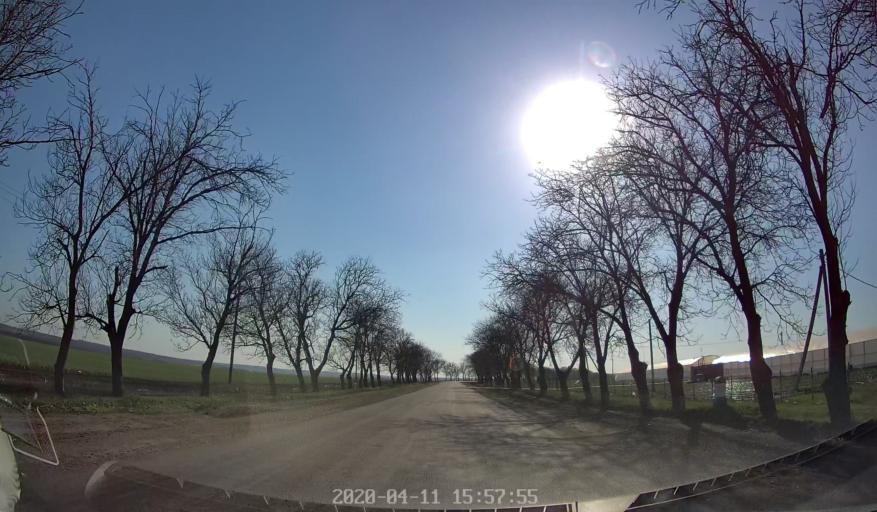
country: MD
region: Chisinau
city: Vadul lui Voda
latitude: 47.0870
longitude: 29.1636
